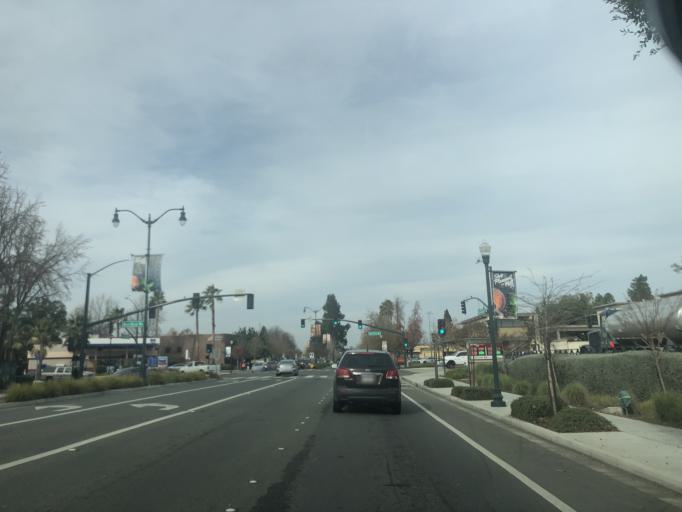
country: US
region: California
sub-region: Contra Costa County
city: Pacheco
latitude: 37.9710
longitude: -122.0634
